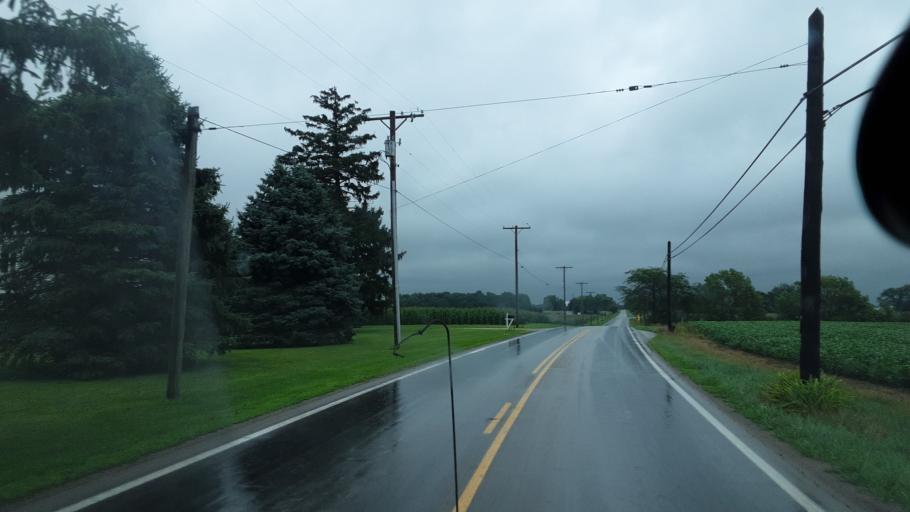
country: US
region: Ohio
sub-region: Mercer County
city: Rockford
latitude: 40.7498
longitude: -84.7822
